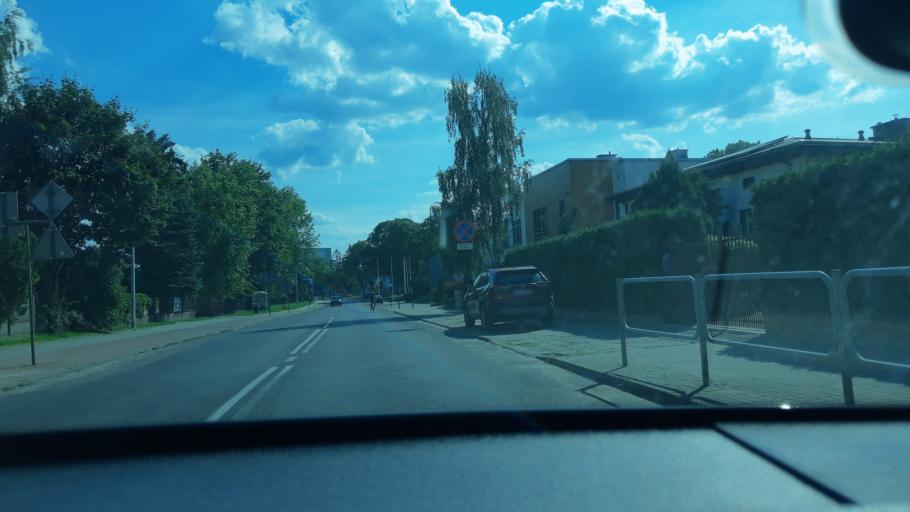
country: PL
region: Lodz Voivodeship
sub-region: Powiat sieradzki
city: Sieradz
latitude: 51.5971
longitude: 18.7370
